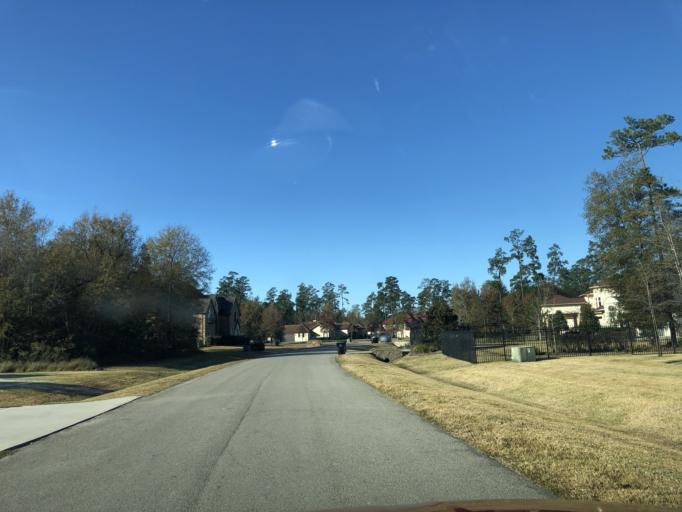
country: US
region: Texas
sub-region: Montgomery County
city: Porter Heights
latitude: 30.0703
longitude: -95.3211
